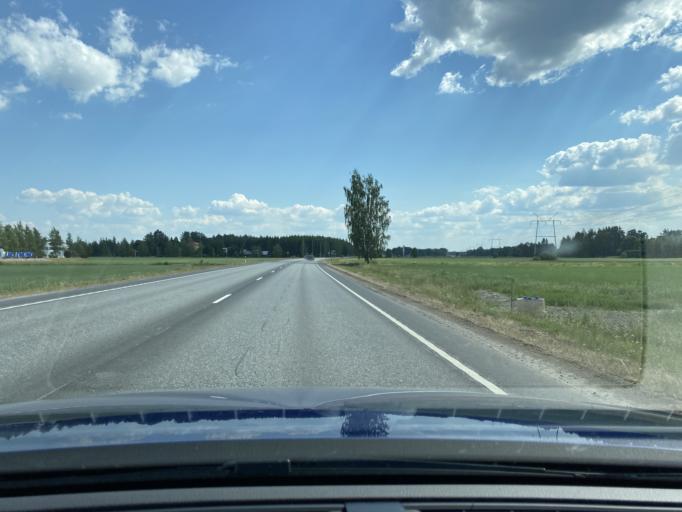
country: FI
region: Satakunta
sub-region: Rauma
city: Eura
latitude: 61.1398
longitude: 22.1153
